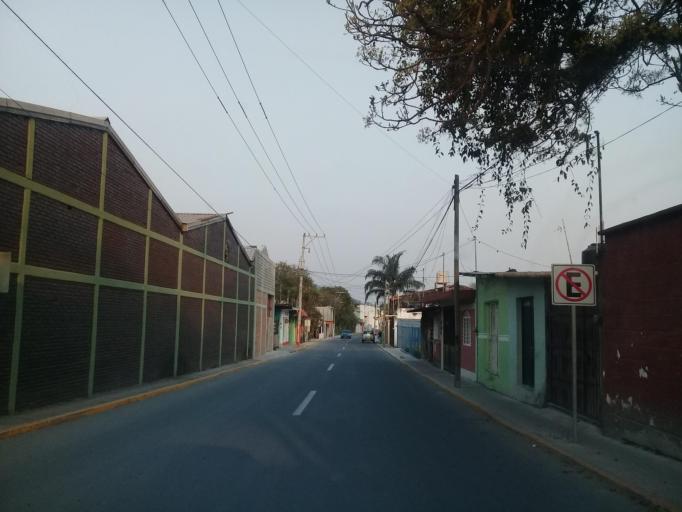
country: MX
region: Veracruz
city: Ixtac Zoquitlan
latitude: 18.8526
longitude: -97.0573
